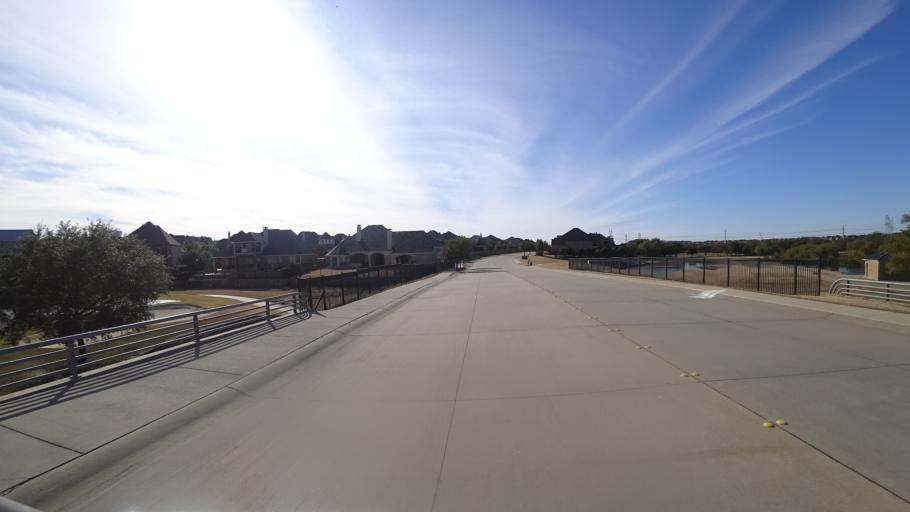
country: US
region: Texas
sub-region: Denton County
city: The Colony
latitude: 33.0305
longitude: -96.9065
